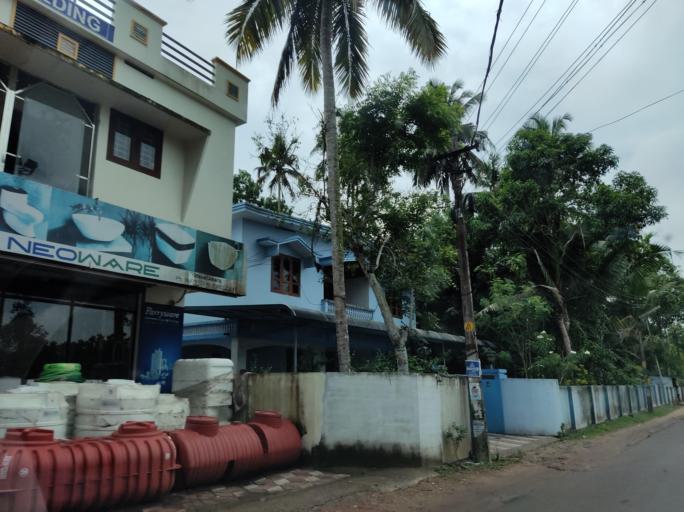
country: IN
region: Kerala
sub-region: Alappuzha
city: Mavelikara
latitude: 9.2414
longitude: 76.5284
